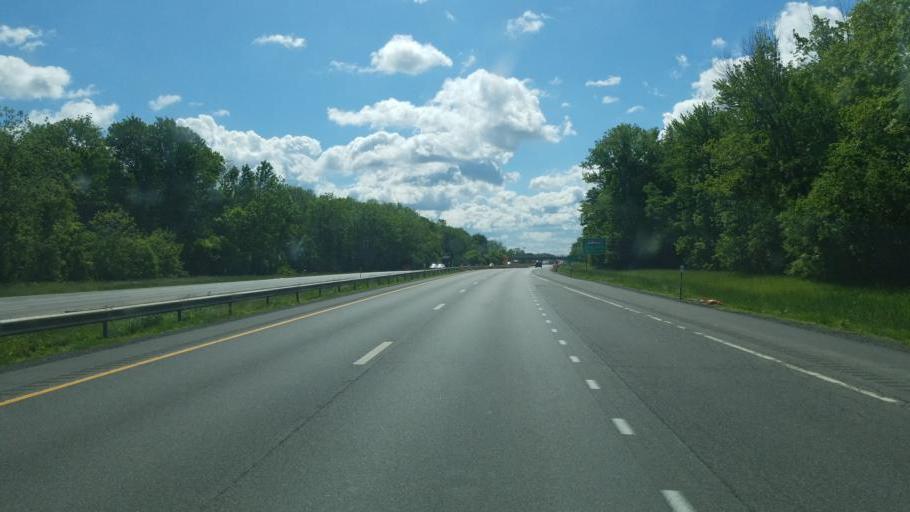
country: US
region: New York
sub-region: Onondaga County
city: Liverpool
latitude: 43.1152
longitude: -76.2120
